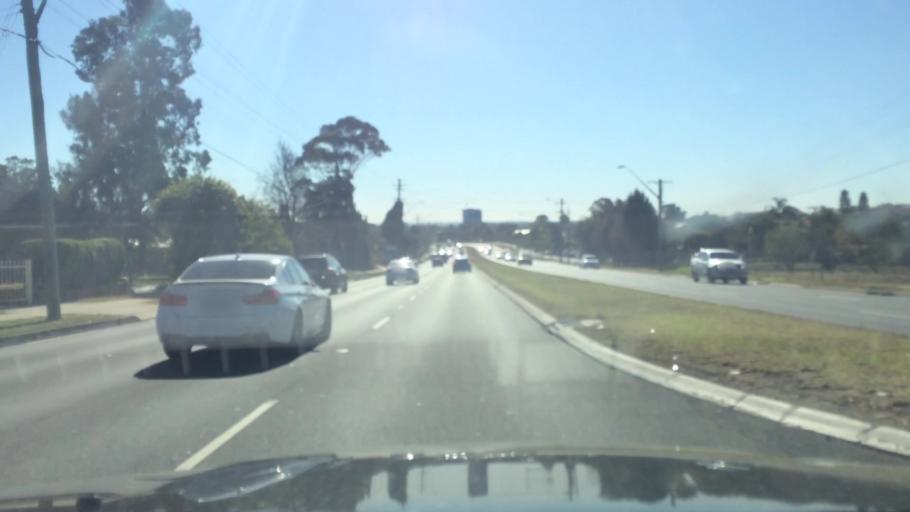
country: AU
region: New South Wales
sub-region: Campbelltown Municipality
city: Glenfield
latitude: -33.9472
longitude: 150.9079
